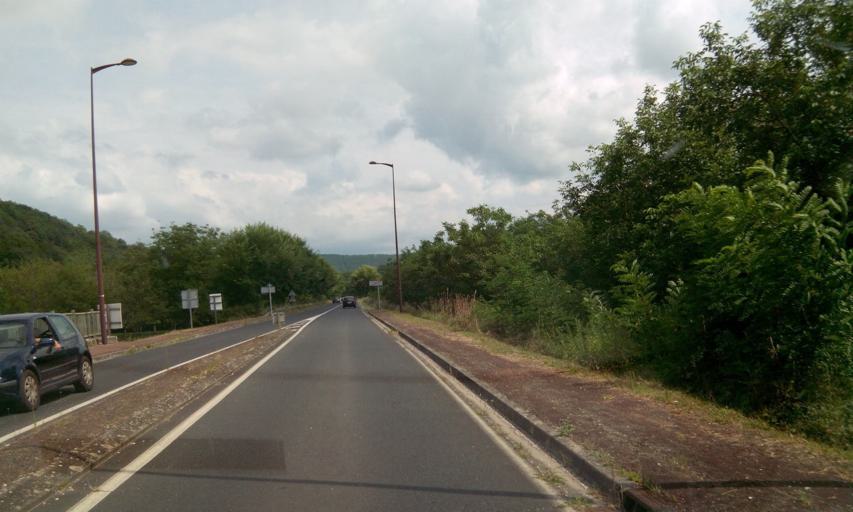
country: FR
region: Midi-Pyrenees
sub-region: Departement du Lot
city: Souillac
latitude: 44.8854
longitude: 1.4090
